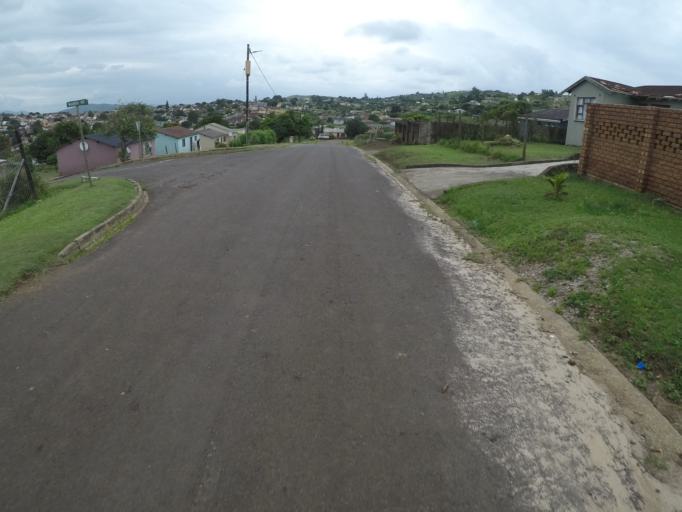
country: ZA
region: KwaZulu-Natal
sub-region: uThungulu District Municipality
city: Empangeni
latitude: -28.7743
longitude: 31.8551
